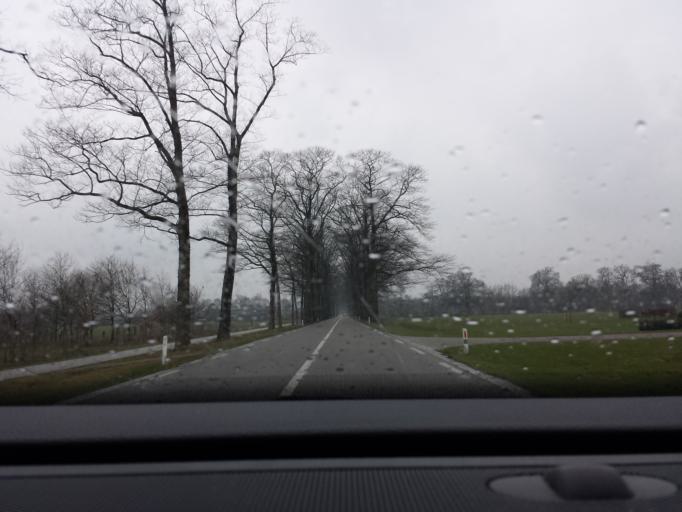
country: NL
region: Gelderland
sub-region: Gemeente Bronckhorst
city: Zelhem
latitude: 52.0038
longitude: 6.3776
